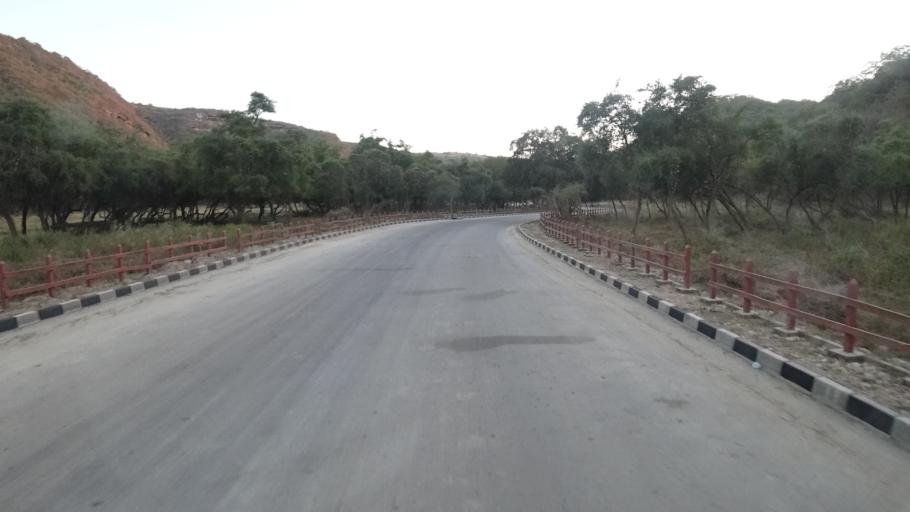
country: OM
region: Zufar
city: Salalah
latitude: 17.0998
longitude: 54.4508
